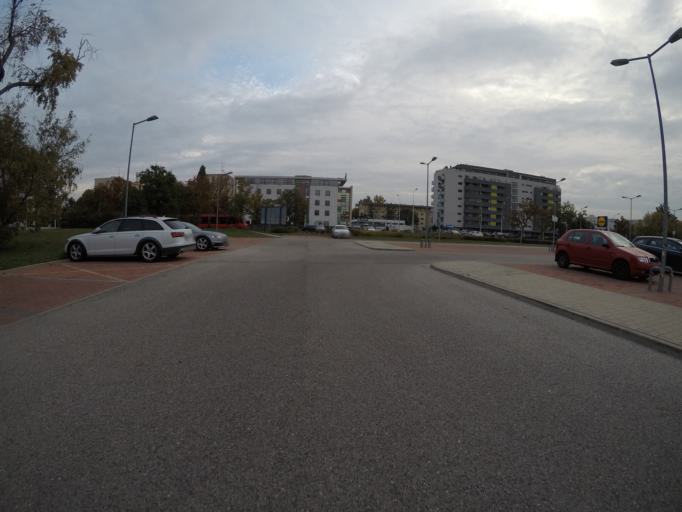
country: SK
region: Bratislavsky
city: Bratislava
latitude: 48.1591
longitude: 17.1744
